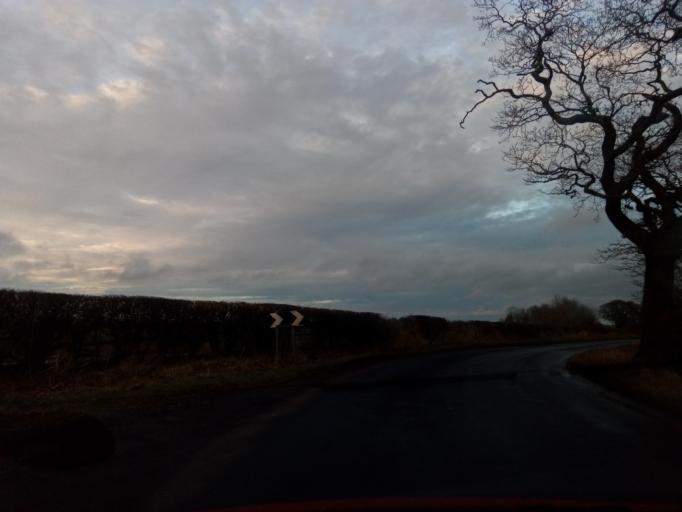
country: GB
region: England
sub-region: Northumberland
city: Ponteland
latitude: 55.0962
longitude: -1.7528
